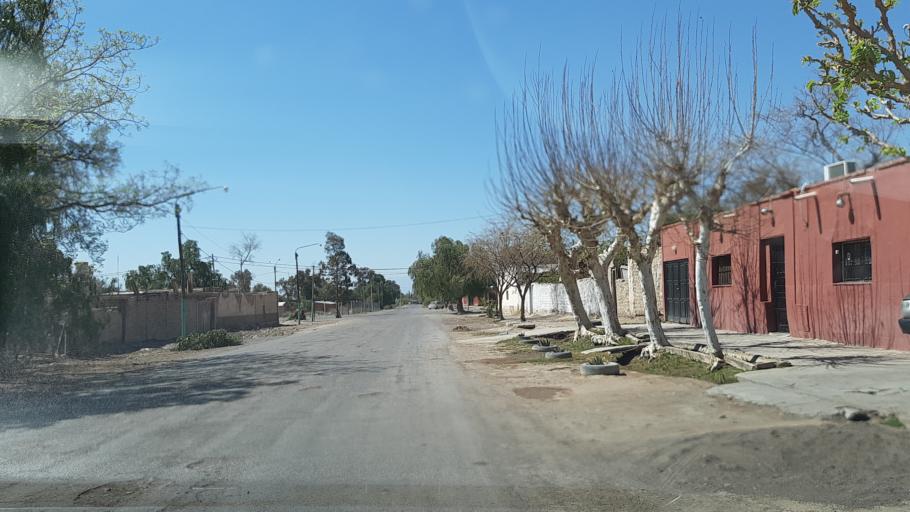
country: AR
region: San Juan
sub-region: Departamento de Rivadavia
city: Rivadavia
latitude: -31.5254
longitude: -68.6324
